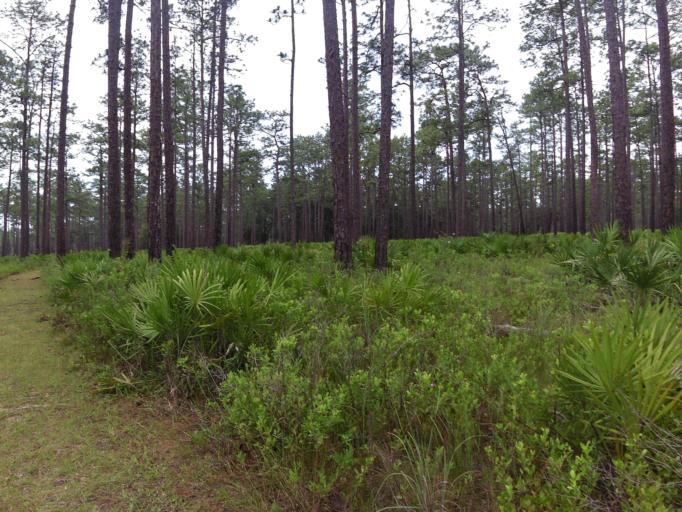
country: US
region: Florida
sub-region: Union County
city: Lake Butler
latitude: 30.2171
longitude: -82.3926
